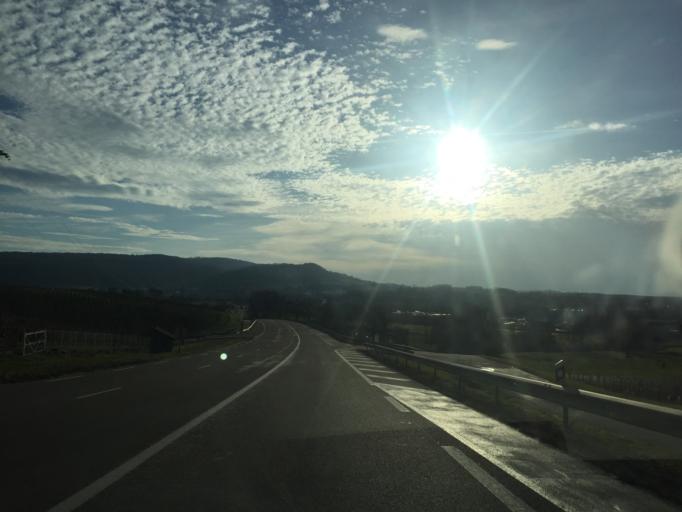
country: FR
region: Franche-Comte
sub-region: Departement du Jura
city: Arbois
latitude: 46.9233
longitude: 5.7737
